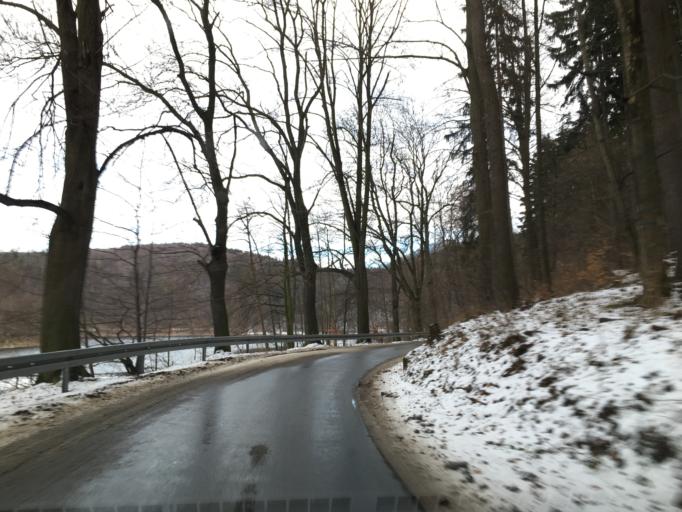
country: PL
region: Lower Silesian Voivodeship
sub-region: Powiat walbrzyski
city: Walim
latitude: 50.7517
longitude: 16.4291
